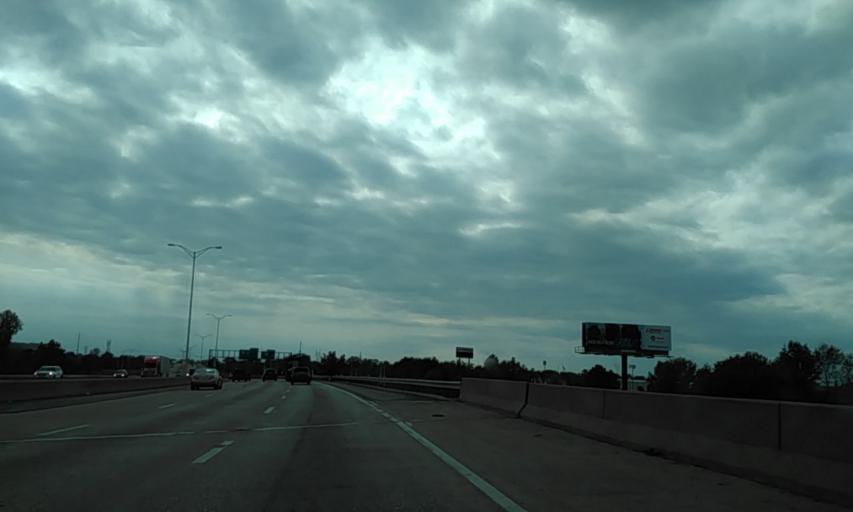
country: US
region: Illinois
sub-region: Saint Clair County
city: Cahokia
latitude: 38.5553
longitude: -90.1555
